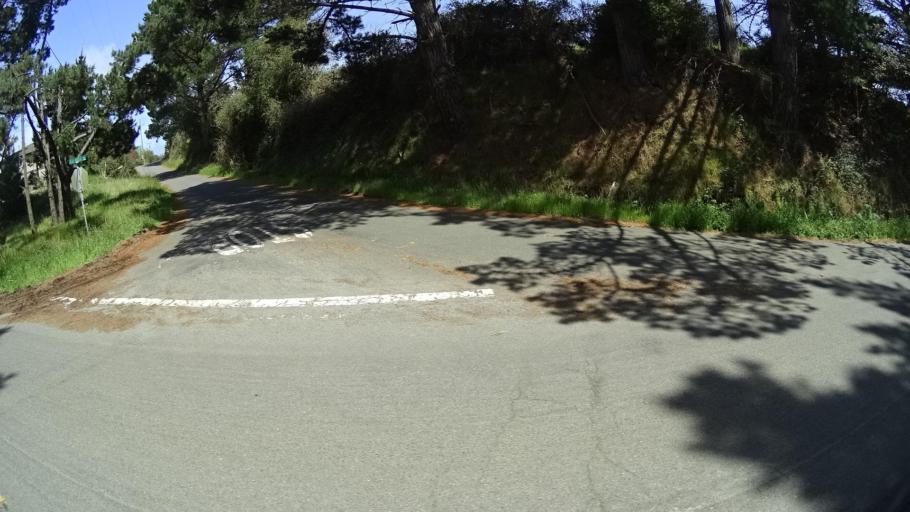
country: US
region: California
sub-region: Humboldt County
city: Ferndale
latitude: 40.6378
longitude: -124.2250
